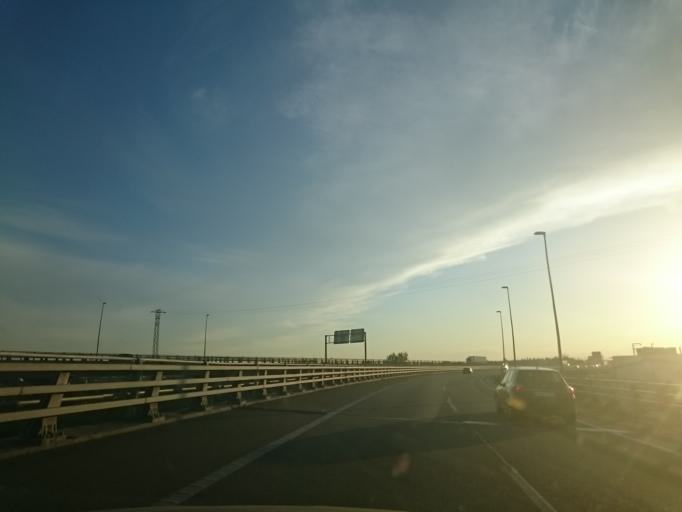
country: ES
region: Catalonia
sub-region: Provincia de Barcelona
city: Montmelo
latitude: 41.5494
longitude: 2.2331
